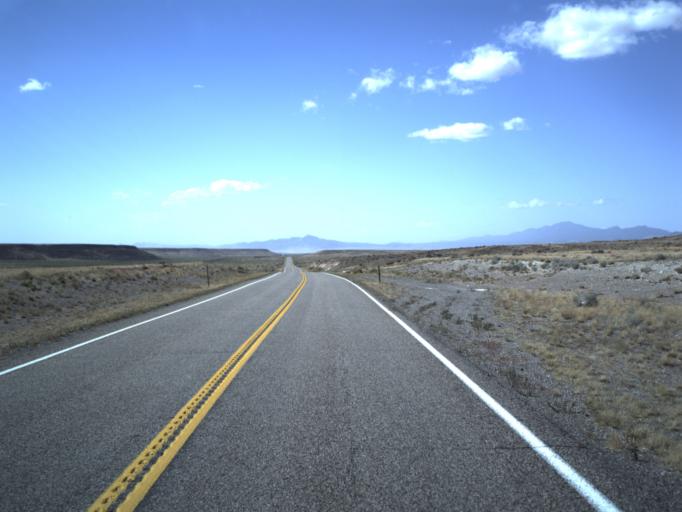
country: US
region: Utah
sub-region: Beaver County
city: Milford
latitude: 38.7698
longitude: -112.9348
